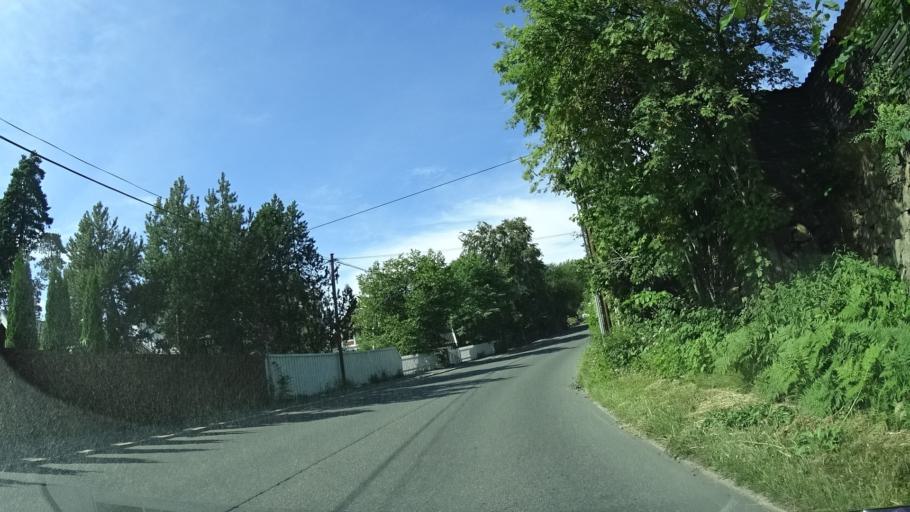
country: NO
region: Oslo
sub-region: Oslo
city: Sjolyststranda
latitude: 59.9541
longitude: 10.6911
